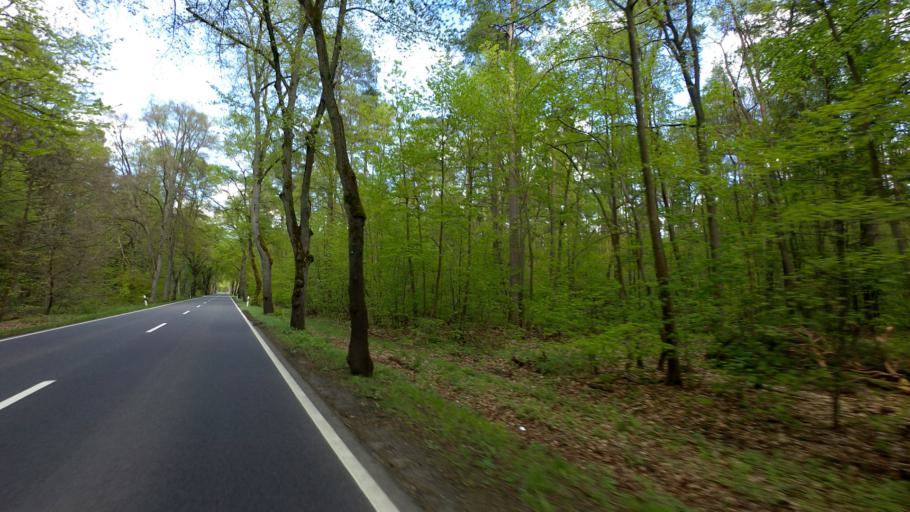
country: DE
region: Brandenburg
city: Friedrichswalde
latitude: 53.0041
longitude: 13.5980
